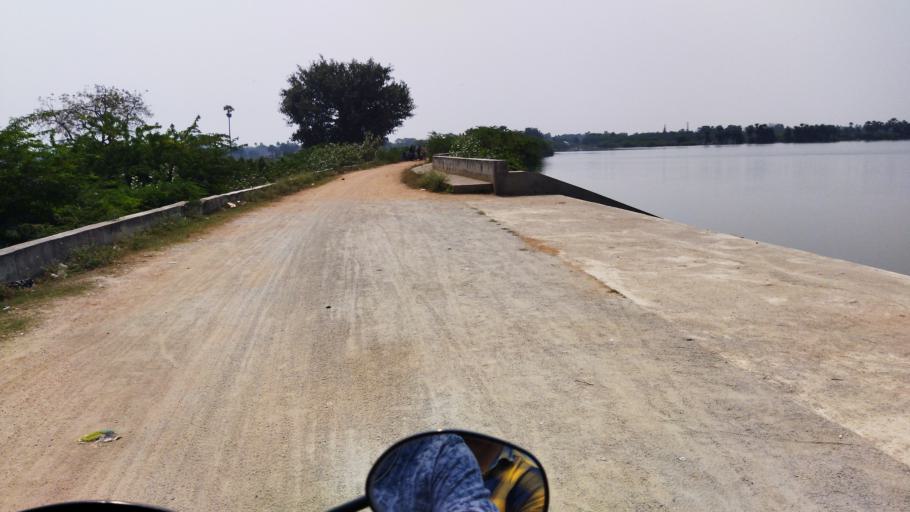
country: IN
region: Telangana
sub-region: Nalgonda
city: Nalgonda
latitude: 17.1647
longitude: 79.4207
